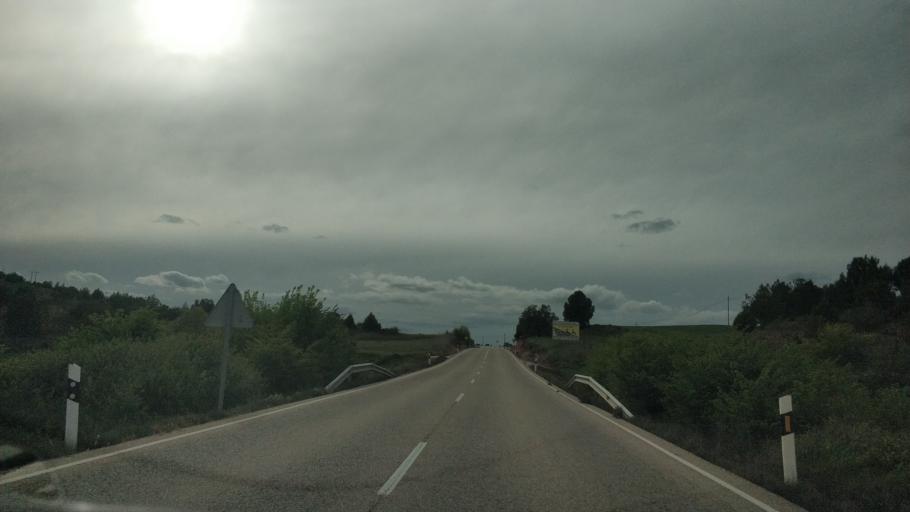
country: ES
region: Castille and Leon
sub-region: Provincia de Soria
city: El Burgo de Osma
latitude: 41.5727
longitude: -3.0163
